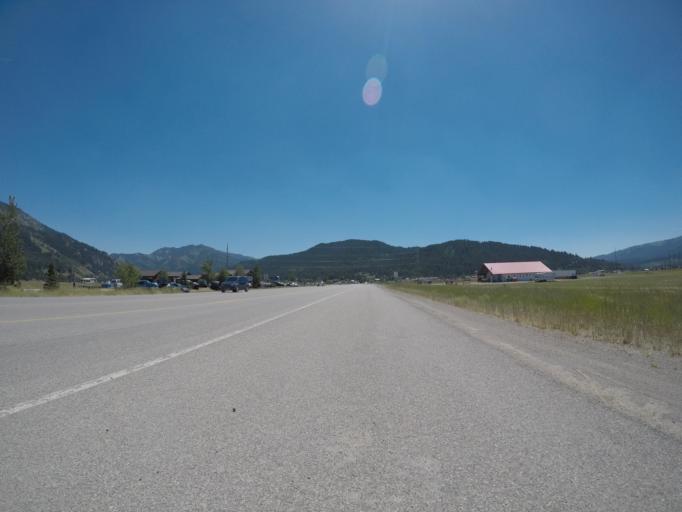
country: US
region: Wyoming
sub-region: Teton County
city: Hoback
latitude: 43.1703
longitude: -111.0182
